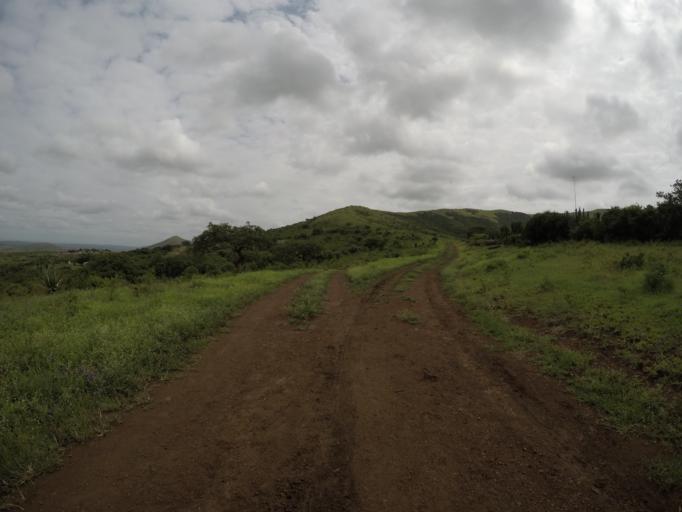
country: ZA
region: KwaZulu-Natal
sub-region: uThungulu District Municipality
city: Empangeni
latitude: -28.6123
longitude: 31.8993
